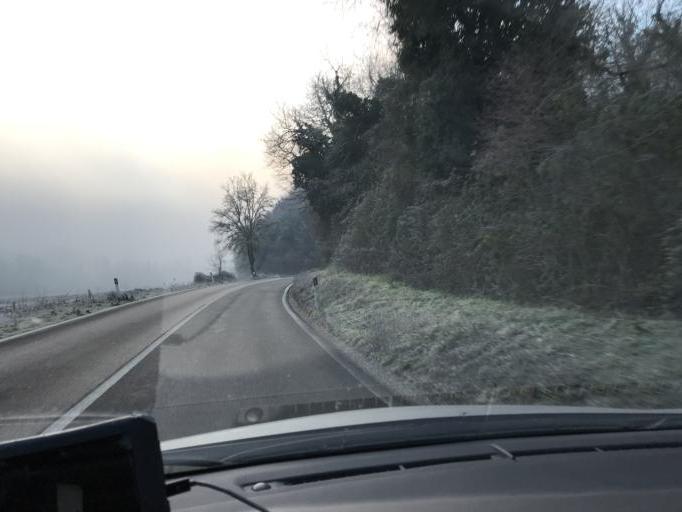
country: IT
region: Latium
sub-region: Provincia di Rieti
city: Colli sul Velino
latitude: 42.5195
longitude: 12.7349
